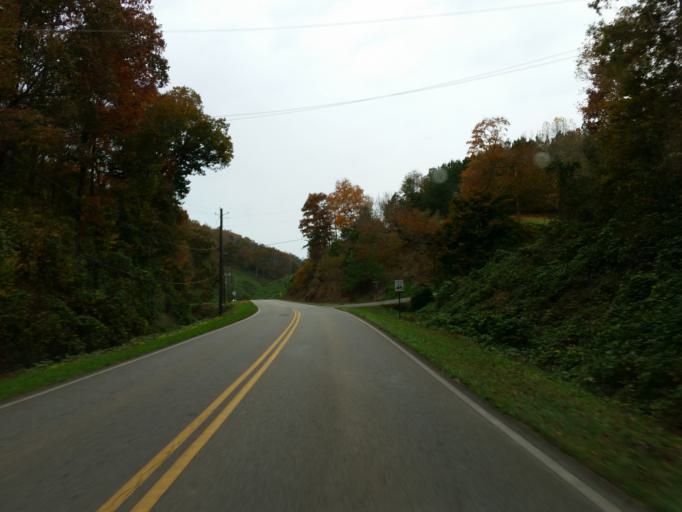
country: US
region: Georgia
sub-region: Pickens County
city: Jasper
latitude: 34.4948
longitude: -84.4288
